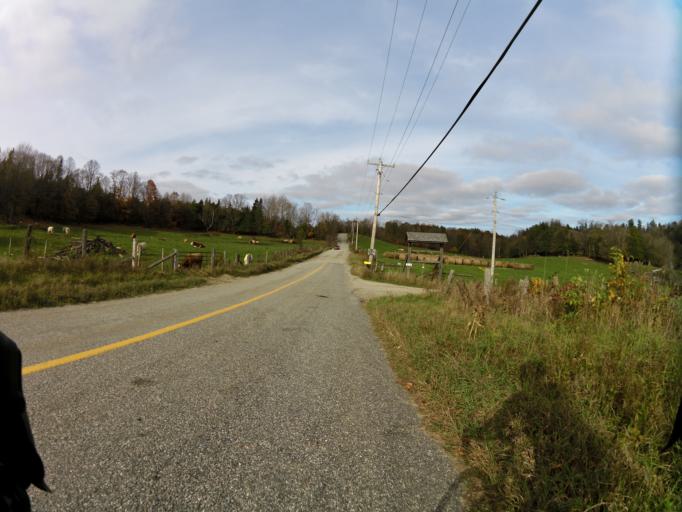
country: CA
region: Quebec
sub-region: Outaouais
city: Wakefield
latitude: 45.7348
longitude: -75.9735
